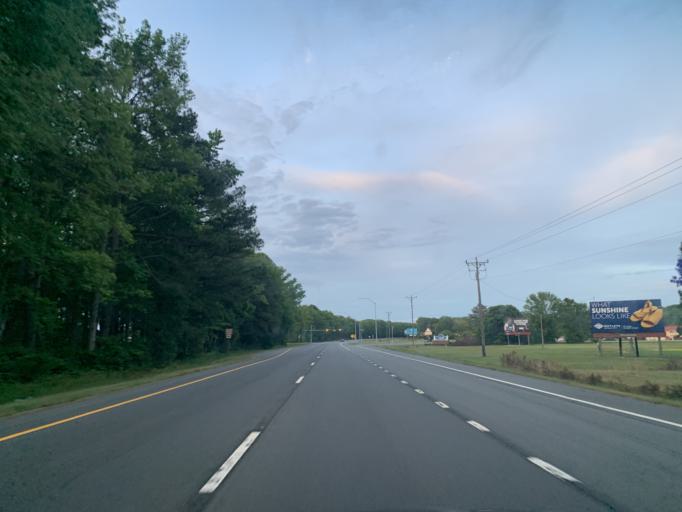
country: US
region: Maryland
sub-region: Wicomico County
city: Pittsville
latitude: 38.3850
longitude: -75.3143
